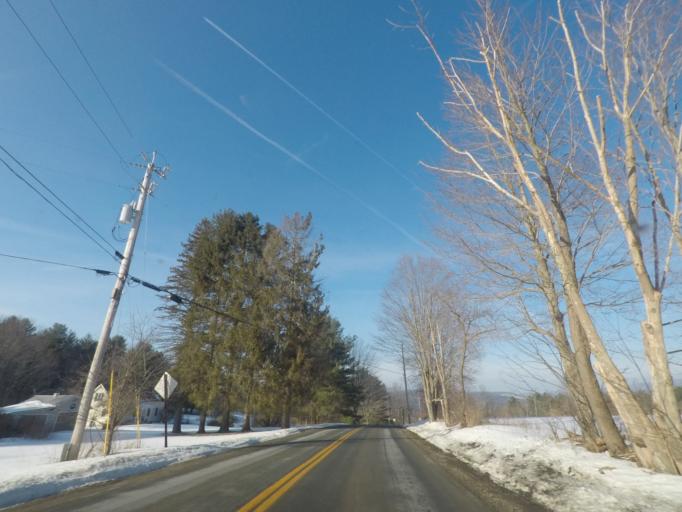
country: US
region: Massachusetts
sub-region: Berkshire County
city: Richmond
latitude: 42.5270
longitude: -73.3938
